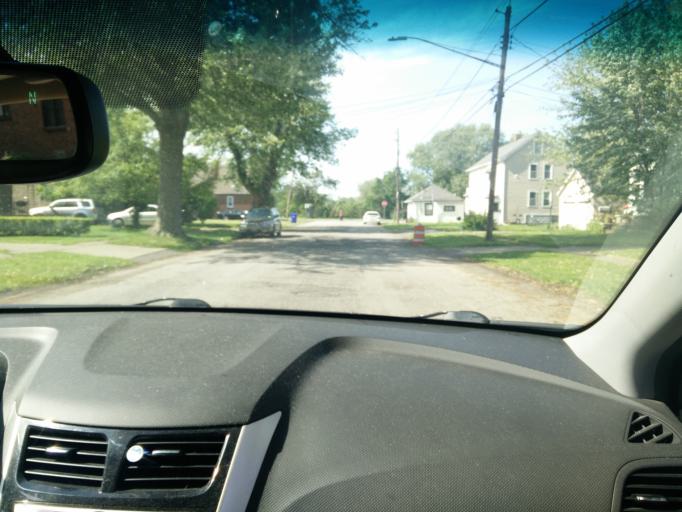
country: US
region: New York
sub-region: Erie County
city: West Seneca
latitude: 42.8376
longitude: -78.7972
